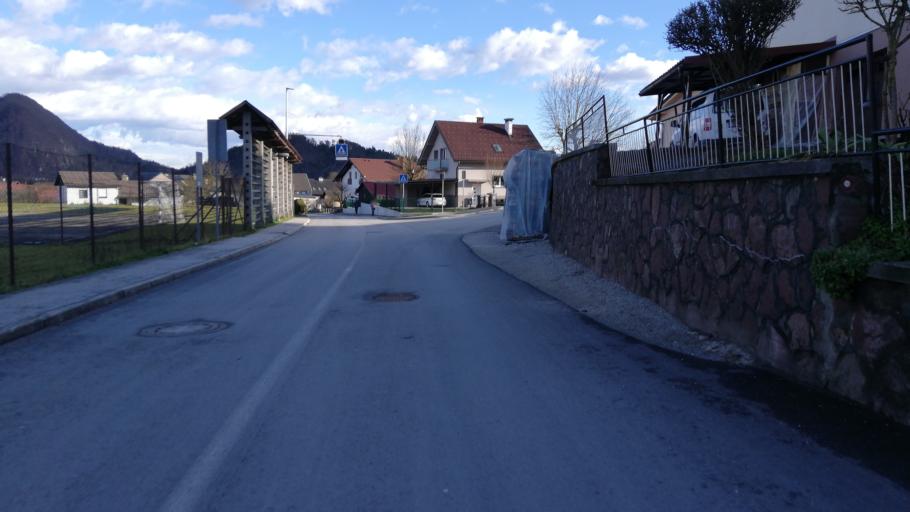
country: SI
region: Medvode
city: Medvode
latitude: 46.1323
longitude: 14.4106
